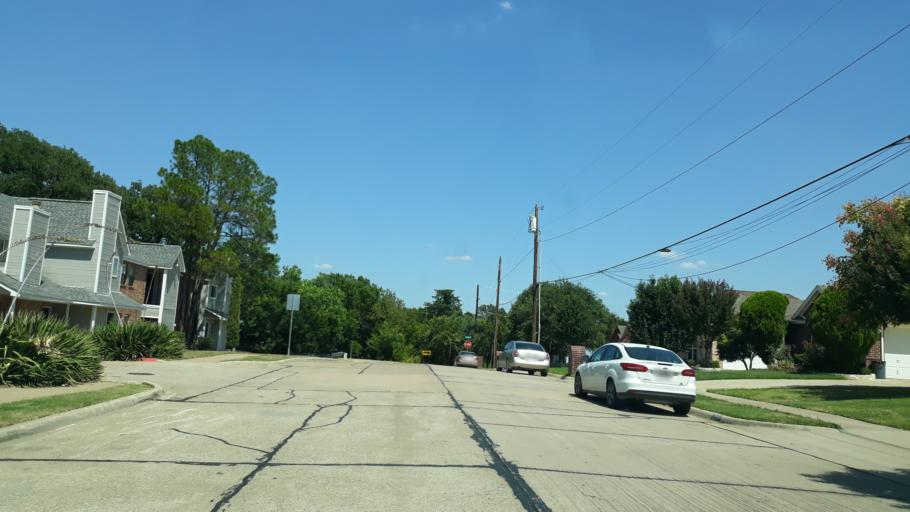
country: US
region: Texas
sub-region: Dallas County
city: Irving
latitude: 32.8266
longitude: -97.0002
